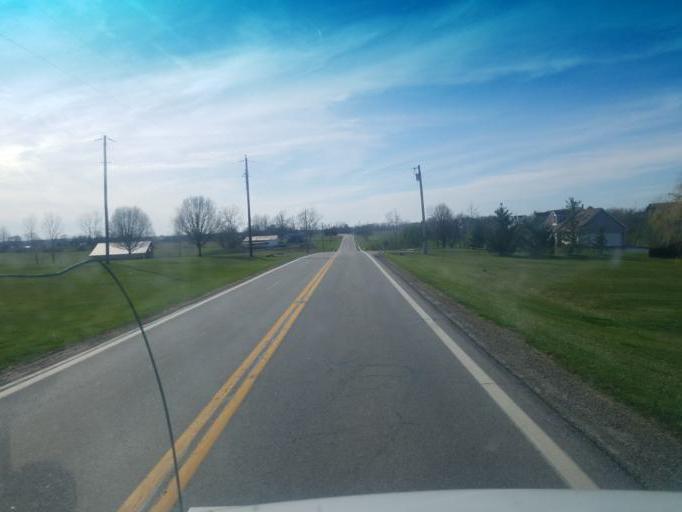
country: US
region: Ohio
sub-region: Champaign County
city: North Lewisburg
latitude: 40.3484
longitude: -83.5087
